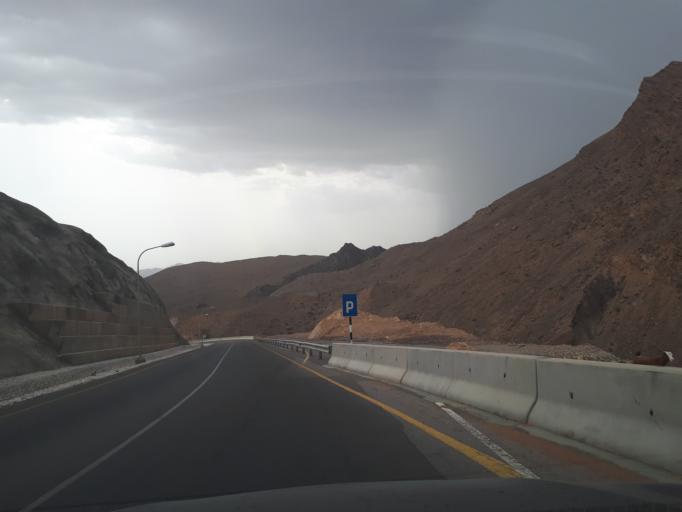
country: OM
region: Ash Sharqiyah
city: Badiyah
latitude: 22.5721
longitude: 59.0713
